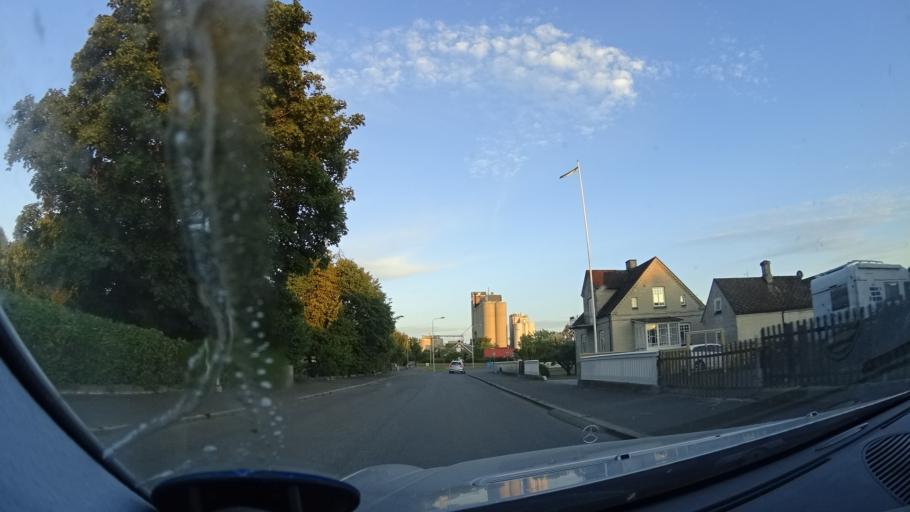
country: SE
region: Skane
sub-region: Kristianstads Kommun
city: Ahus
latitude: 55.9296
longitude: 14.3044
